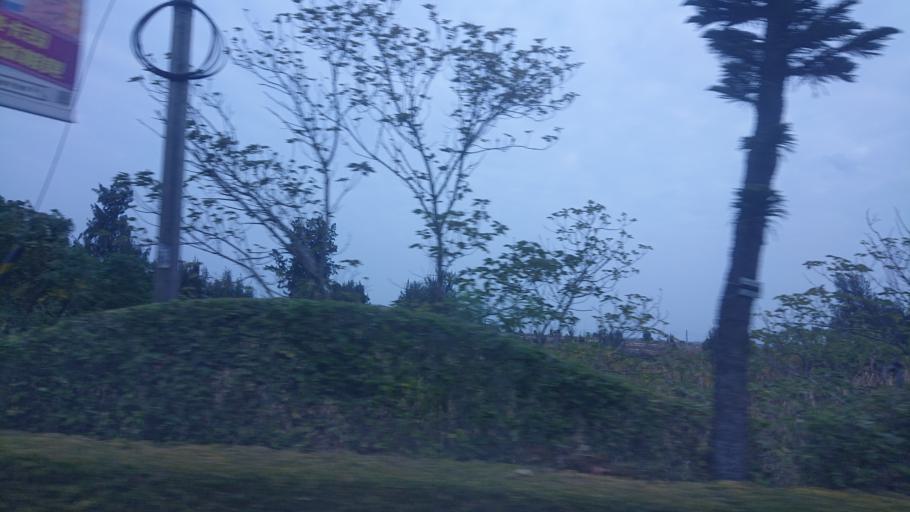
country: TW
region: Fukien
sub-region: Kinmen
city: Jincheng
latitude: 24.4125
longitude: 118.2904
